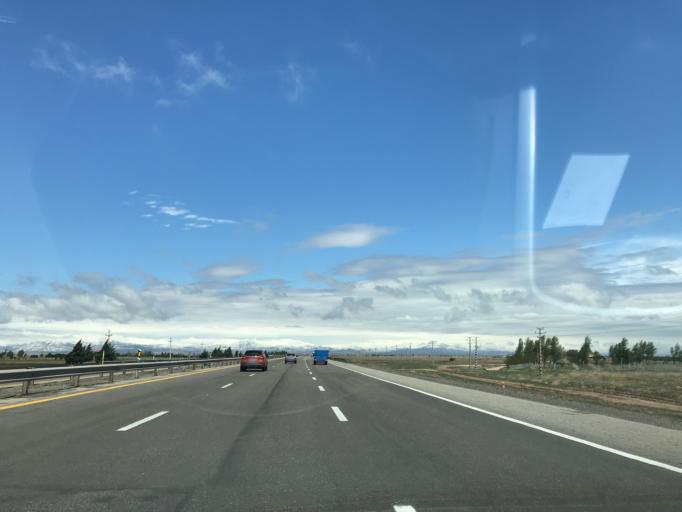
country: IR
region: Qazvin
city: Takestan
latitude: 36.1542
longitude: 49.7813
